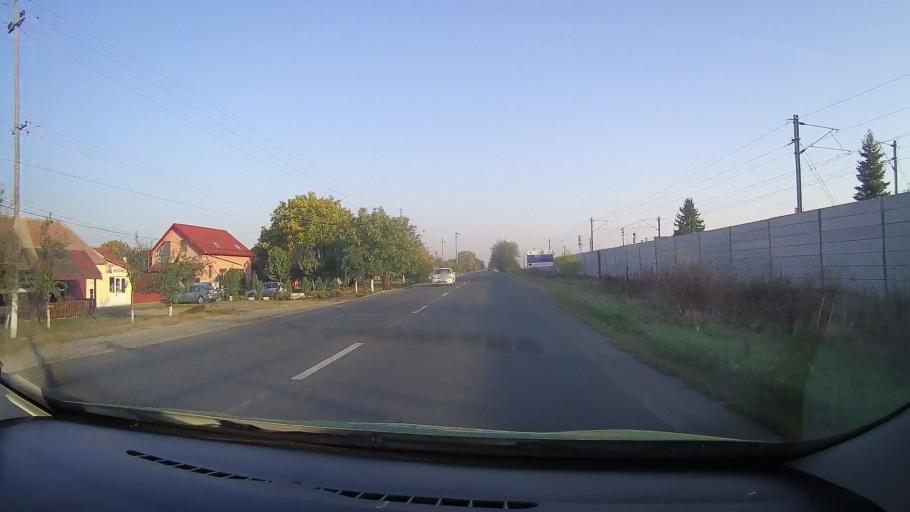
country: RO
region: Arad
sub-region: Comuna Sofronea
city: Sofronea
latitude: 46.2847
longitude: 21.3130
